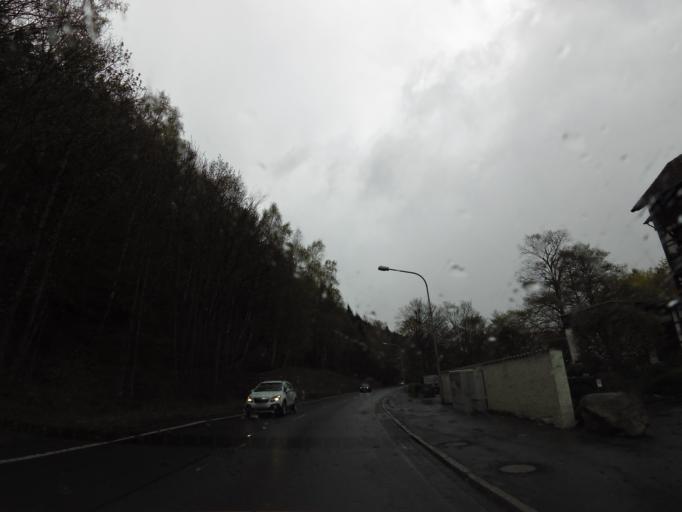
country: DE
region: Lower Saxony
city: Goslar
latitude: 51.8902
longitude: 10.4759
